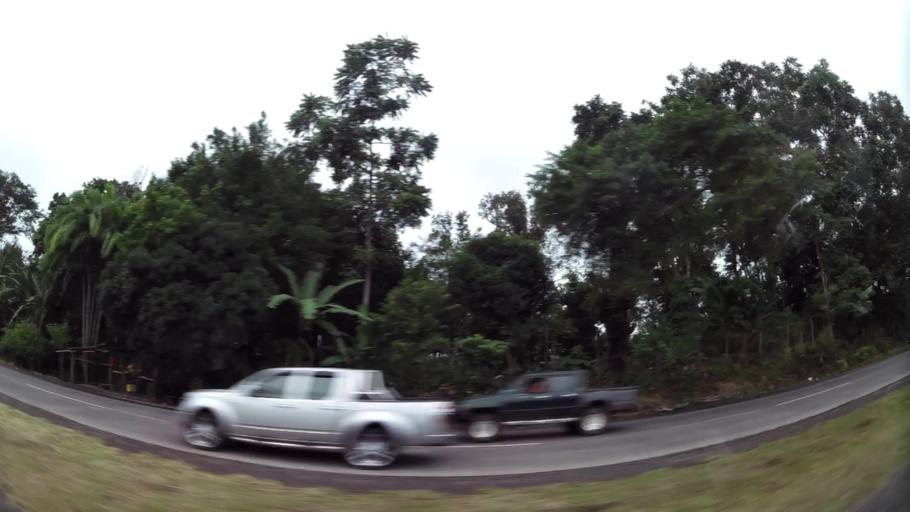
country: PA
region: Chiriqui
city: La Concepcion
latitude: 8.5075
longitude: -82.6115
